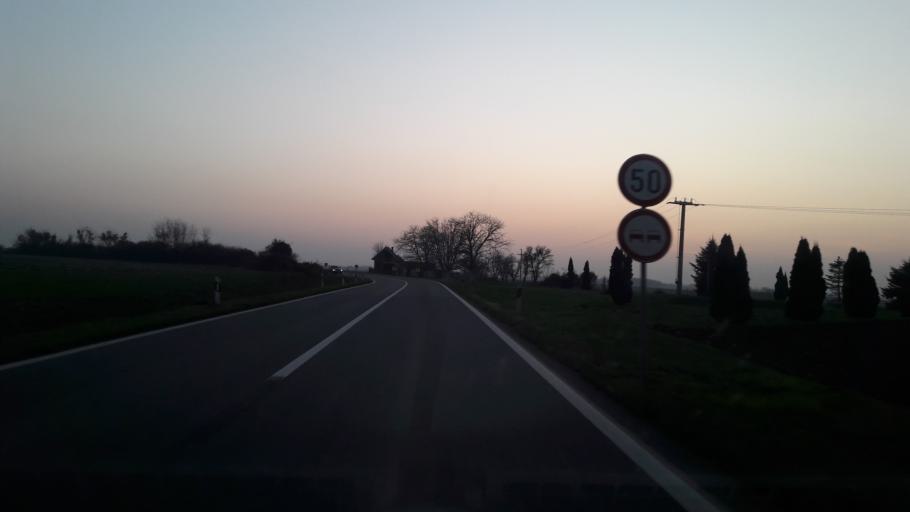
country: HR
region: Vukovarsko-Srijemska
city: Negoslavci
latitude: 45.2634
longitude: 18.9880
